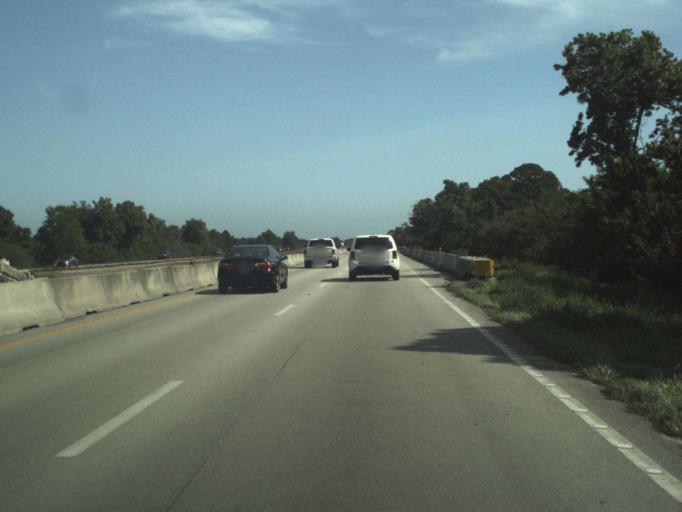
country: US
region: Florida
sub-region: Indian River County
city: Fellsmere
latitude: 27.7188
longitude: -80.5442
